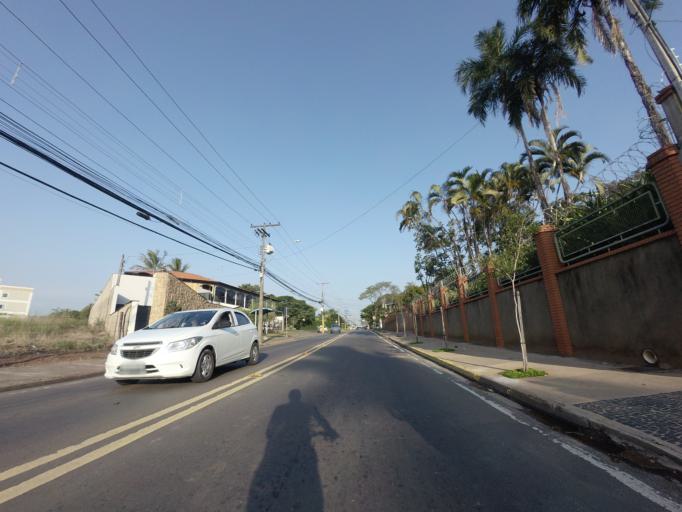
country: BR
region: Sao Paulo
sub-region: Piracicaba
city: Piracicaba
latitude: -22.7412
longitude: -47.6095
